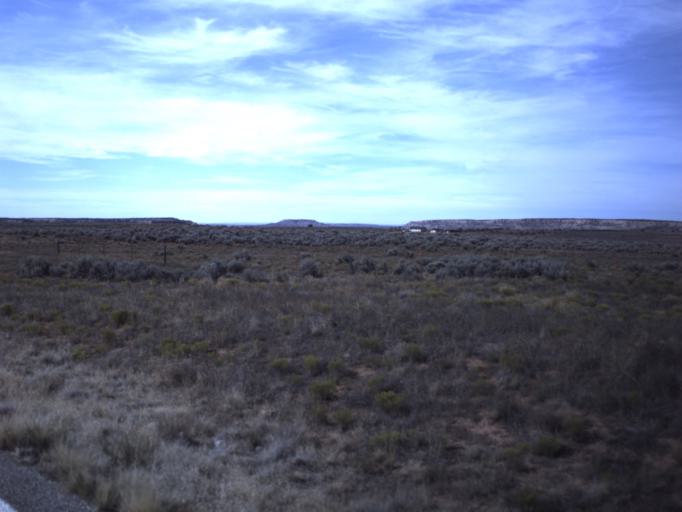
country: US
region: Utah
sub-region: San Juan County
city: Blanding
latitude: 37.3875
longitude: -109.3401
